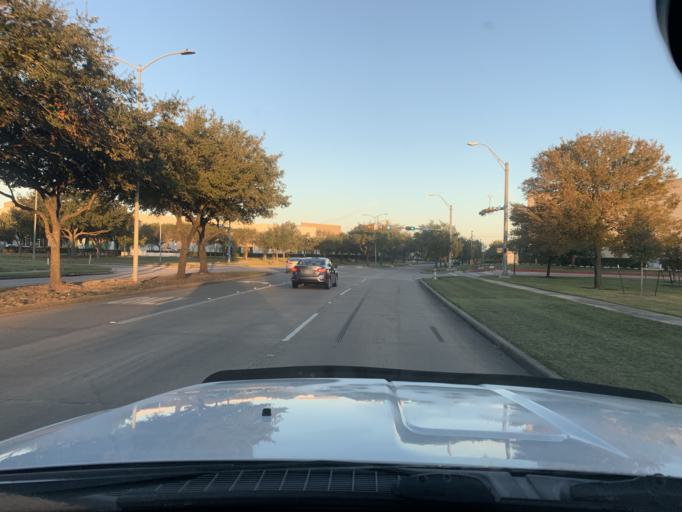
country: US
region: Texas
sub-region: Fort Bend County
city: Meadows Place
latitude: 29.6467
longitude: -95.6116
